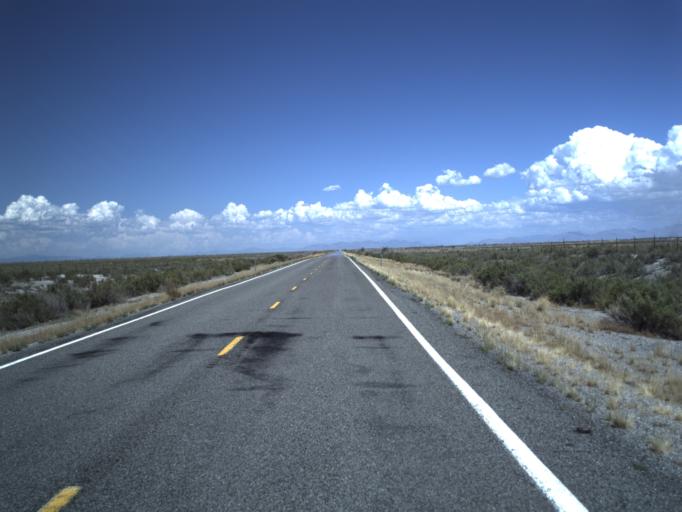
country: US
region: Utah
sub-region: Millard County
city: Delta
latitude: 39.2866
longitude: -112.8350
